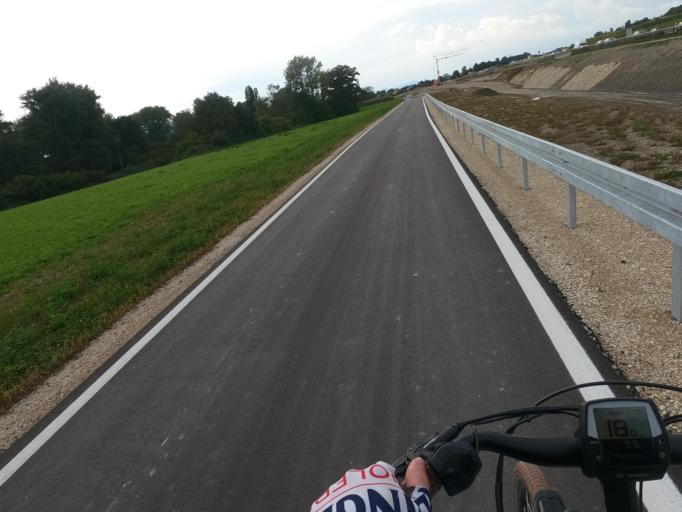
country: DE
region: Baden-Wuerttemberg
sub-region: Freiburg Region
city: Allensbach
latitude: 47.7090
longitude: 9.0919
